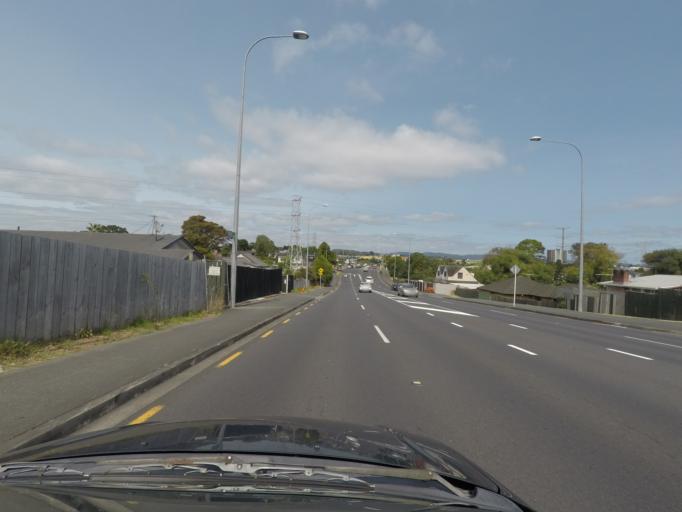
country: NZ
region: Auckland
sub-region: Auckland
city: Waitakere
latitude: -36.9091
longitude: 174.6956
